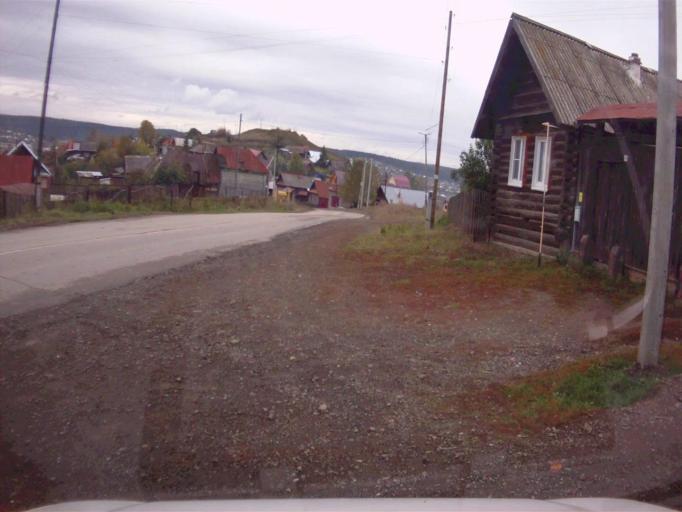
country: RU
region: Chelyabinsk
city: Nyazepetrovsk
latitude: 56.0611
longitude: 59.6144
